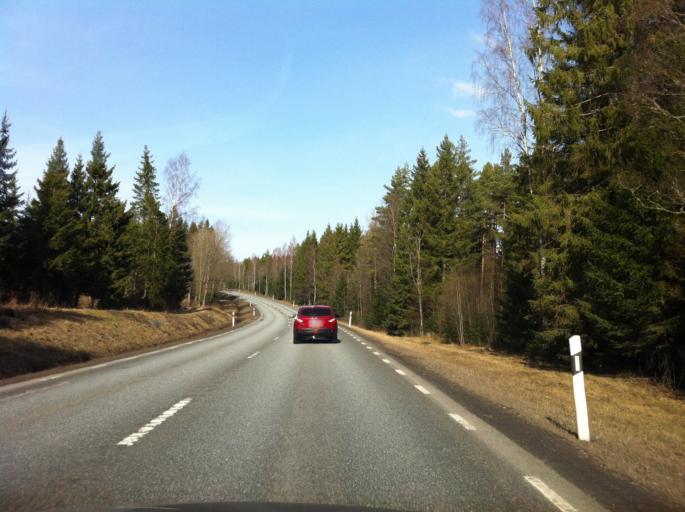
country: SE
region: Joenkoeping
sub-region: Mullsjo Kommun
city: Mullsjoe
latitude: 58.0083
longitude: 13.8307
